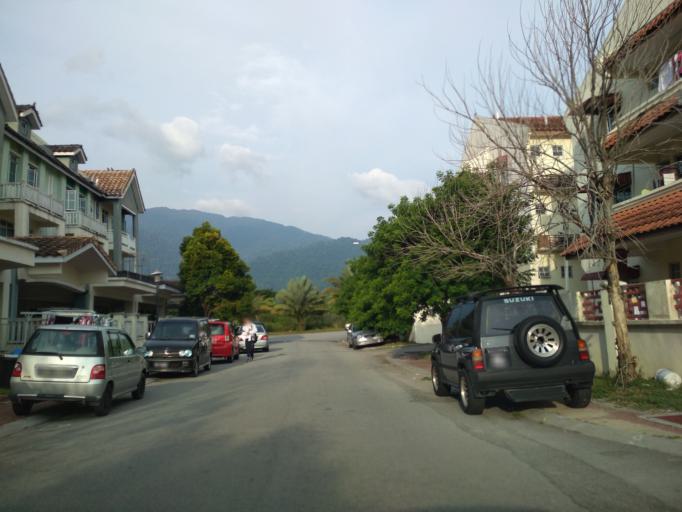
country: MY
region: Perak
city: Kampar
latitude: 4.3297
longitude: 101.1381
